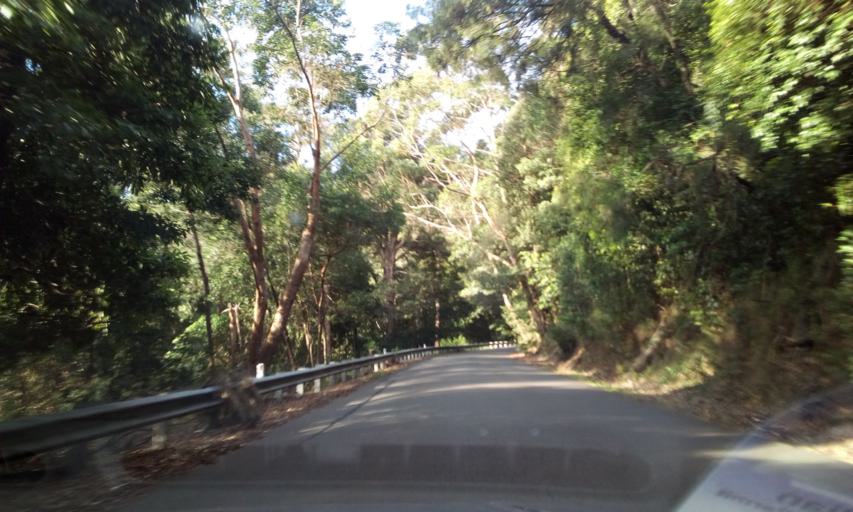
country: AU
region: New South Wales
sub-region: Wollongong
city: Mount Keira
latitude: -34.4006
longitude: 150.8503
